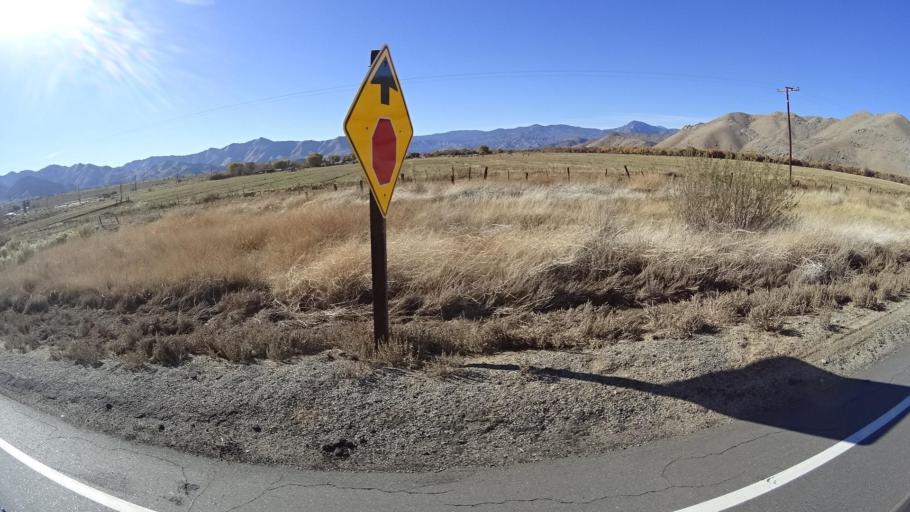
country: US
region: California
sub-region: Kern County
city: Weldon
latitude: 35.6593
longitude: -118.3223
